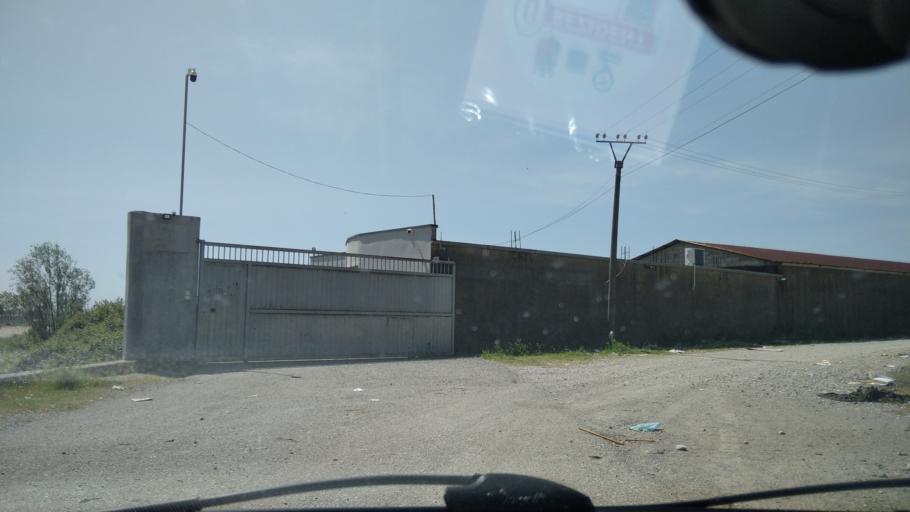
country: AL
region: Shkoder
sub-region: Rrethi i Malesia e Madhe
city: Kuc
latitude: 42.0503
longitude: 19.5212
